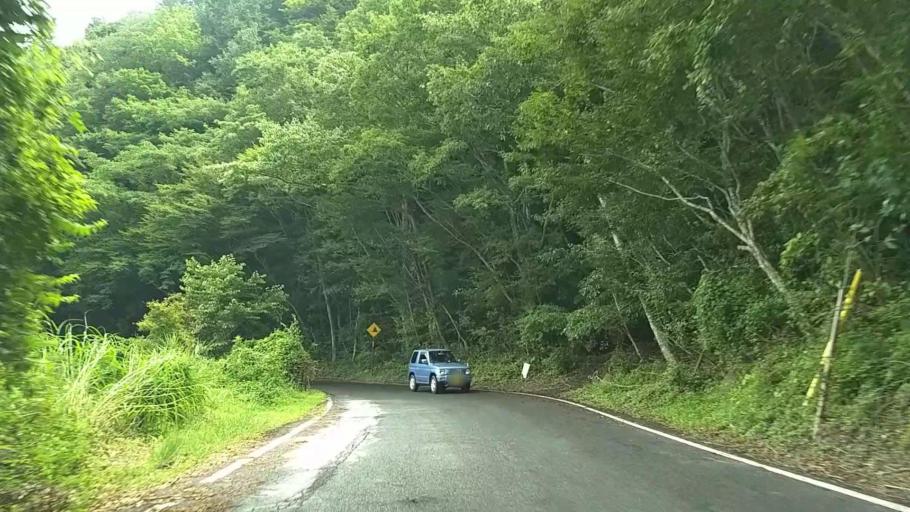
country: JP
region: Yamanashi
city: Fujikawaguchiko
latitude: 35.4669
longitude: 138.5749
